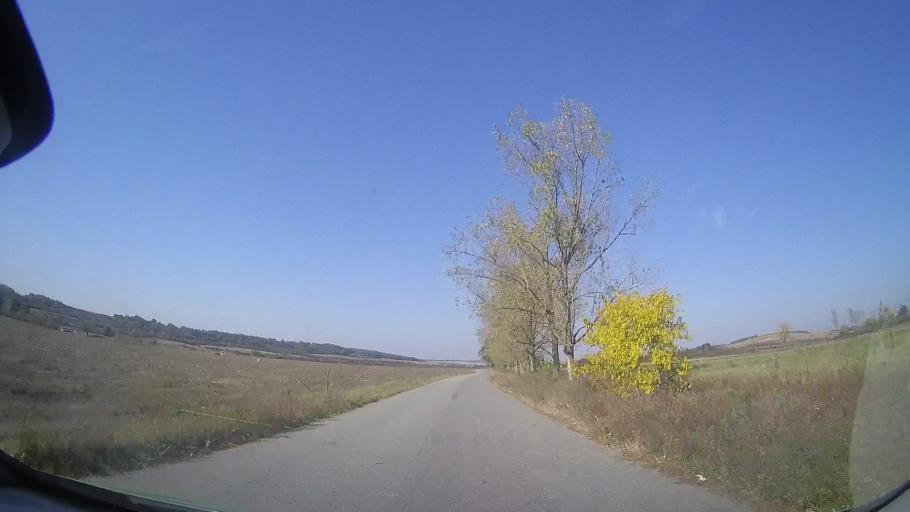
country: RO
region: Timis
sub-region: Comuna Ghizela
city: Ghizela
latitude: 45.8233
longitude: 21.7299
